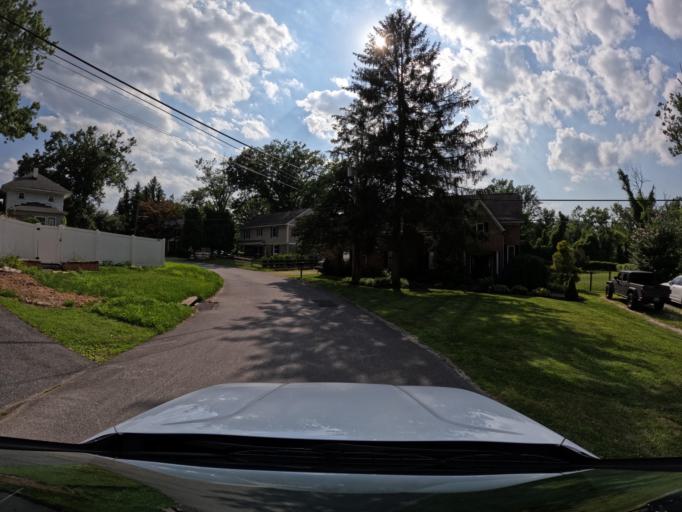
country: US
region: Maryland
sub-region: Baltimore County
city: Mays Chapel
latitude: 39.4107
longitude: -76.6467
